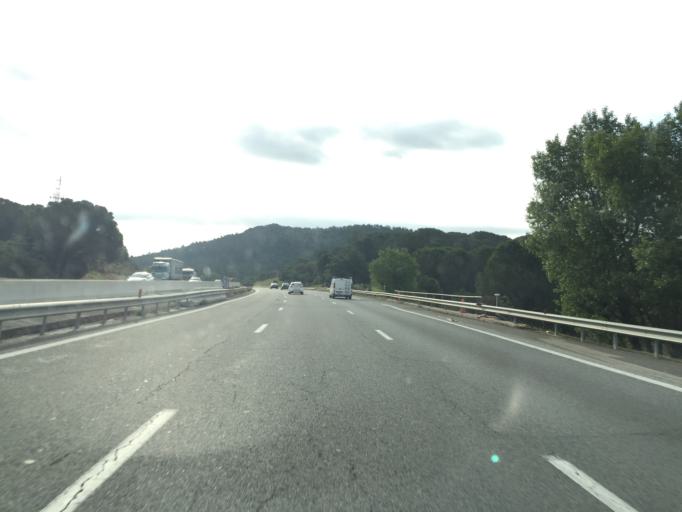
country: FR
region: Provence-Alpes-Cote d'Azur
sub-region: Departement du Var
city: Les Arcs
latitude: 43.4517
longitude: 6.5165
